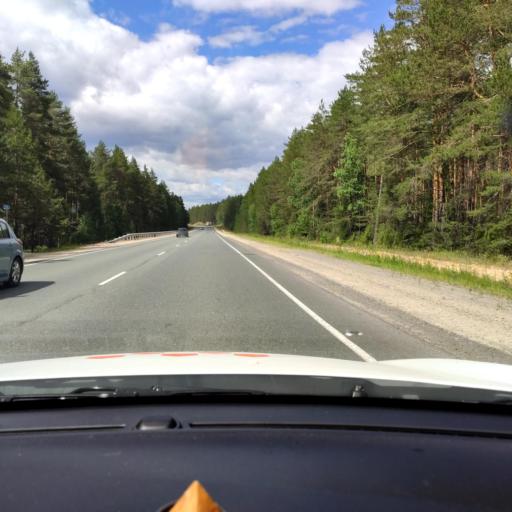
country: RU
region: Mariy-El
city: Pomary
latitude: 56.0559
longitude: 48.3727
